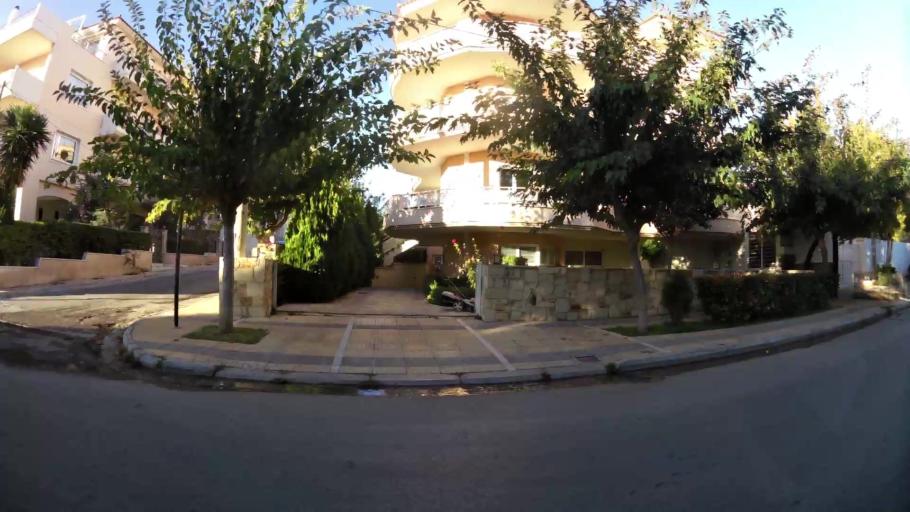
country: GR
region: Attica
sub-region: Nomarchia Anatolikis Attikis
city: Spata
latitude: 37.9589
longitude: 23.9159
